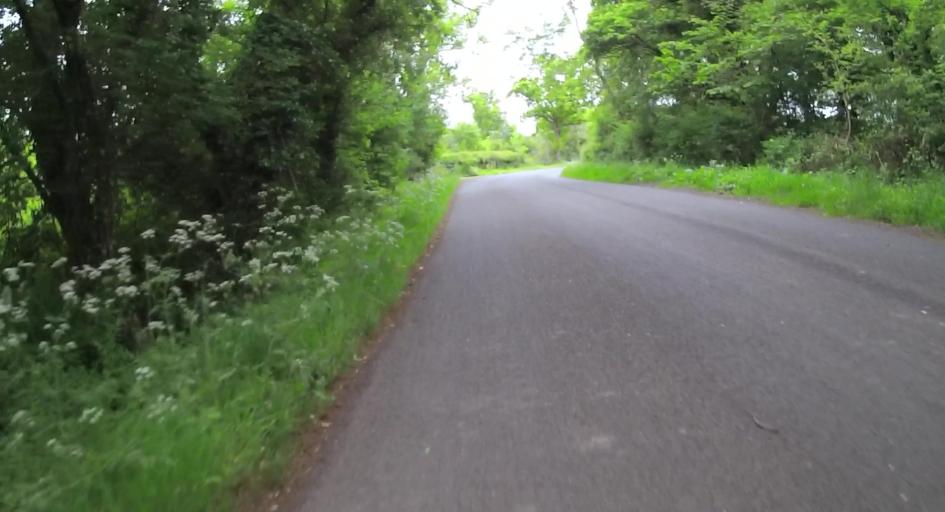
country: GB
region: England
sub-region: West Berkshire
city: Stratfield Mortimer
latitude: 51.3656
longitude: -1.0358
